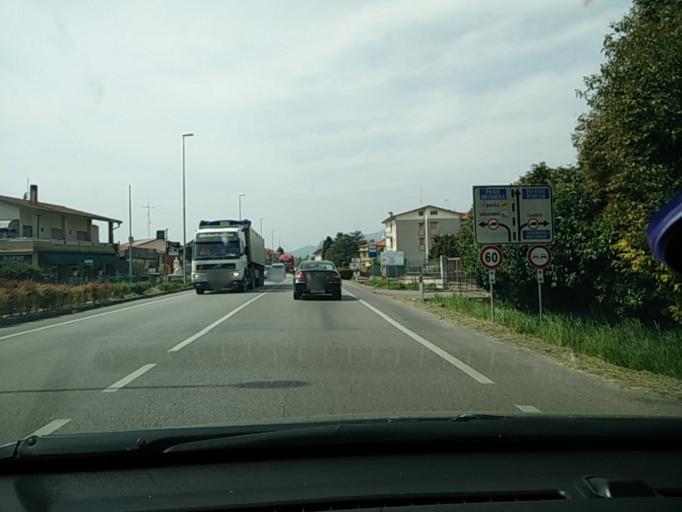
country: IT
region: Friuli Venezia Giulia
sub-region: Provincia di Pordenone
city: Vigonovo-Fontanafredda
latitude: 45.9717
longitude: 12.5750
